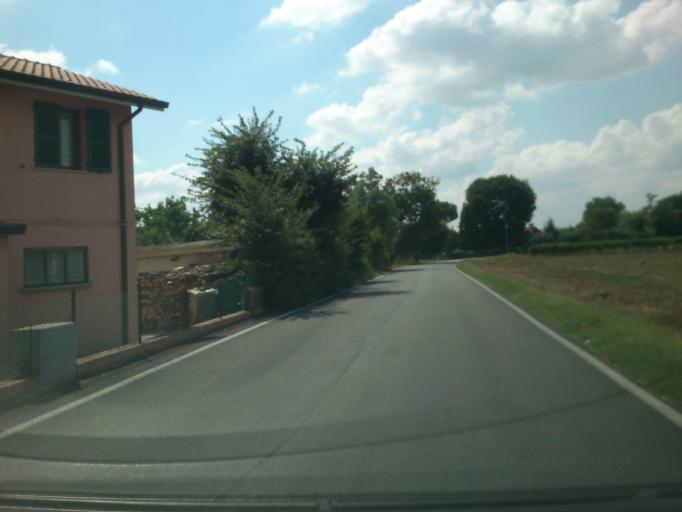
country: IT
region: The Marches
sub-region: Provincia di Pesaro e Urbino
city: Bellocchi
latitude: 43.7991
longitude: 12.9869
